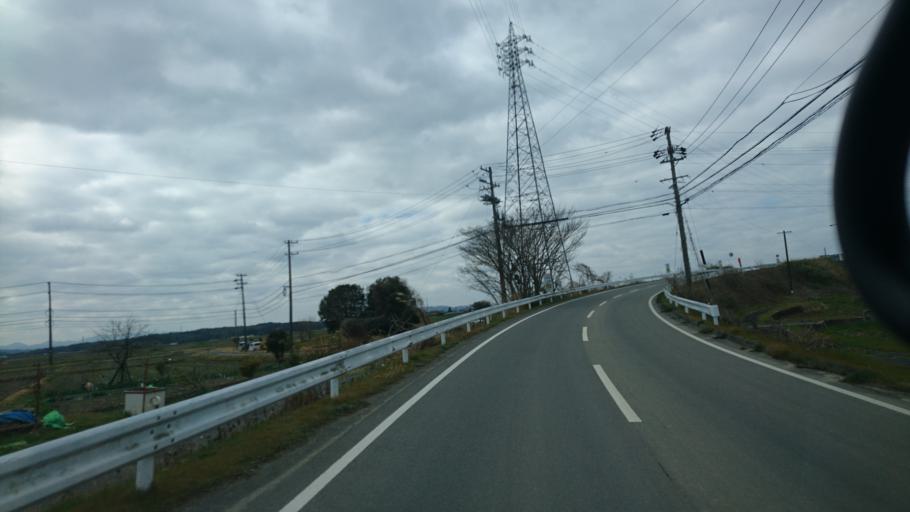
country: JP
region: Mie
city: Ueno-ebisumachi
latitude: 34.7520
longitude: 136.1191
